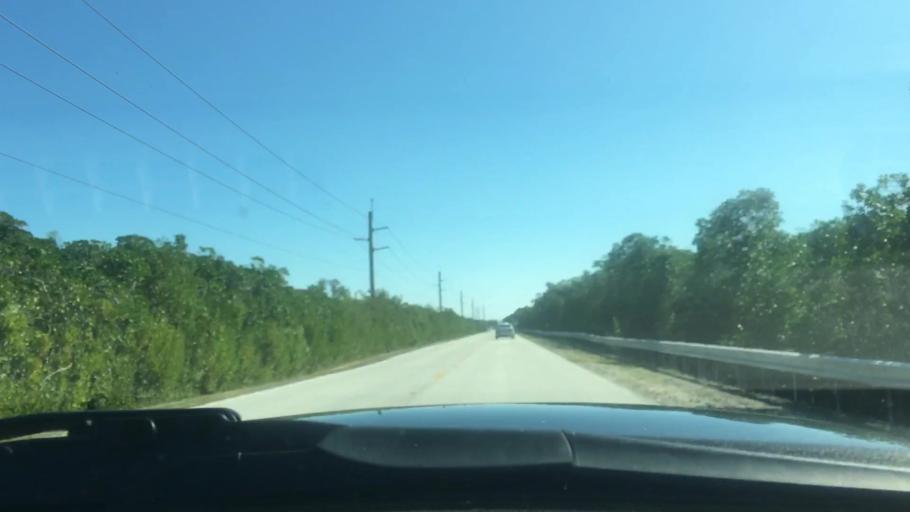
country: US
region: Florida
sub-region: Monroe County
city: North Key Largo
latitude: 25.2811
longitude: -80.3487
